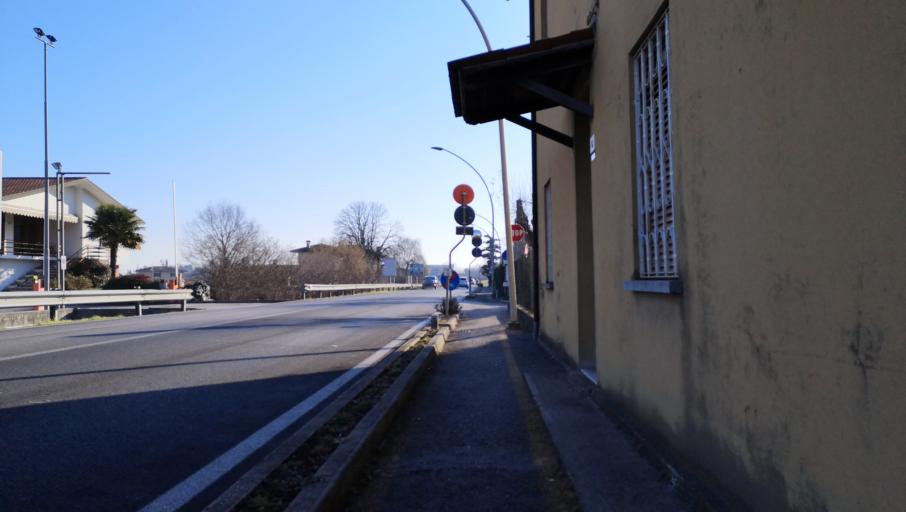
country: IT
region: Friuli Venezia Giulia
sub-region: Provincia di Udine
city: Palmanova
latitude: 45.9106
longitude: 13.2987
